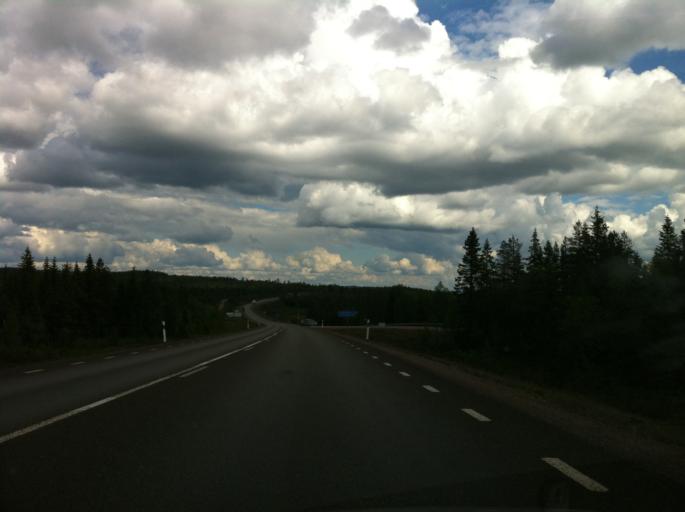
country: SE
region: Dalarna
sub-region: Malung-Saelens kommun
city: Malung
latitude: 60.5181
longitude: 13.4999
